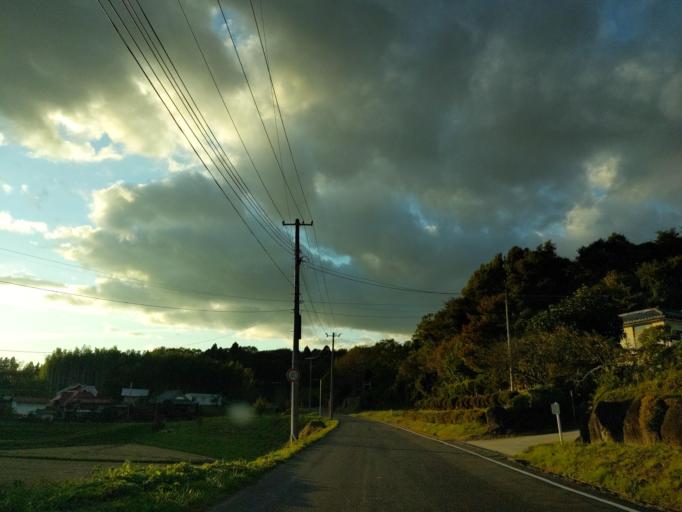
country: JP
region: Fukushima
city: Motomiya
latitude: 37.4762
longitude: 140.4337
